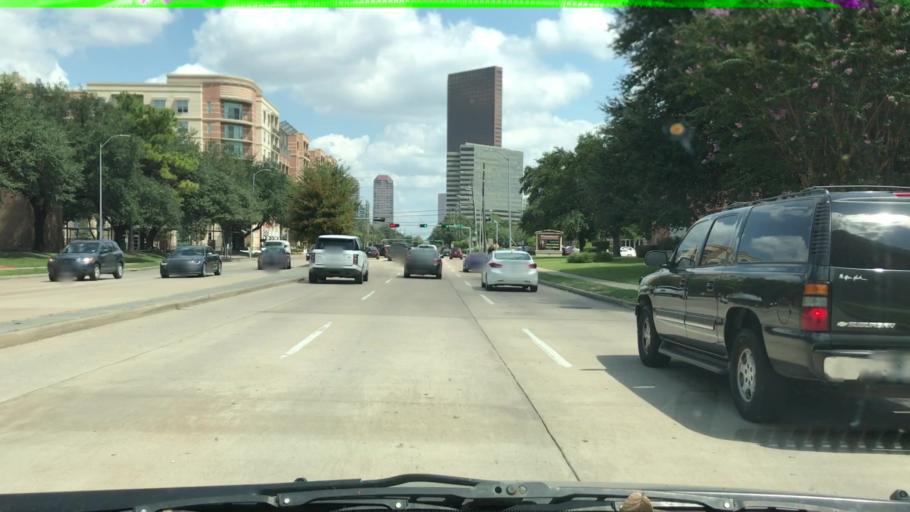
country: US
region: Texas
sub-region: Harris County
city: Hunters Creek Village
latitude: 29.7500
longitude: -95.4809
